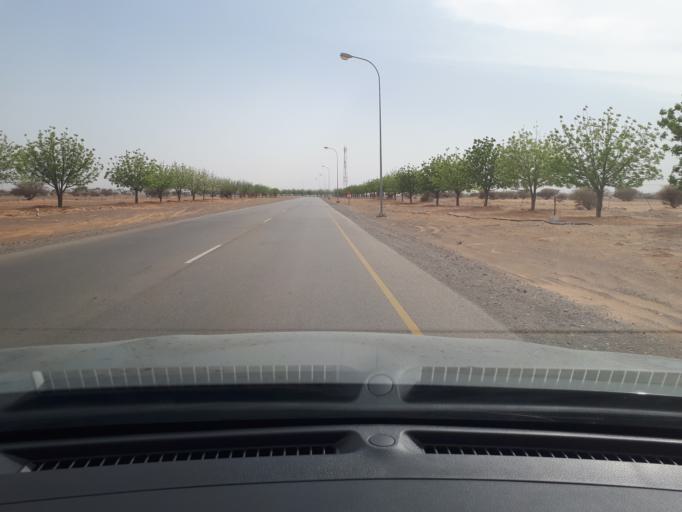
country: OM
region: Ash Sharqiyah
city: Badiyah
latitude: 22.5001
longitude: 58.9418
